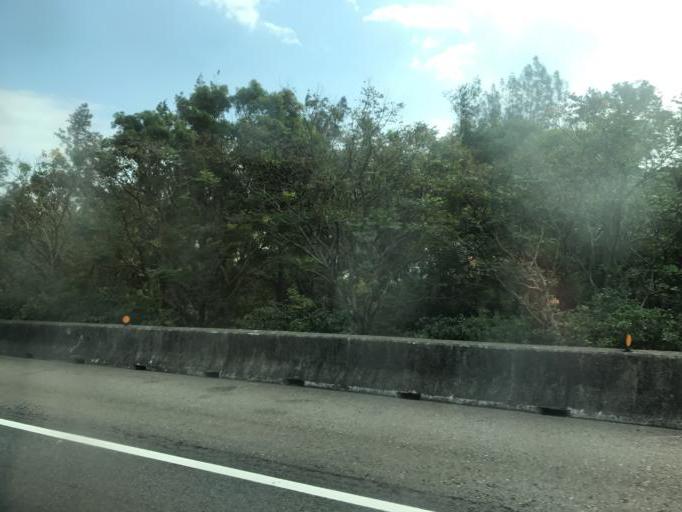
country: TW
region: Taiwan
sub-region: Hsinchu
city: Zhubei
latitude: 24.8769
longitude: 121.0430
